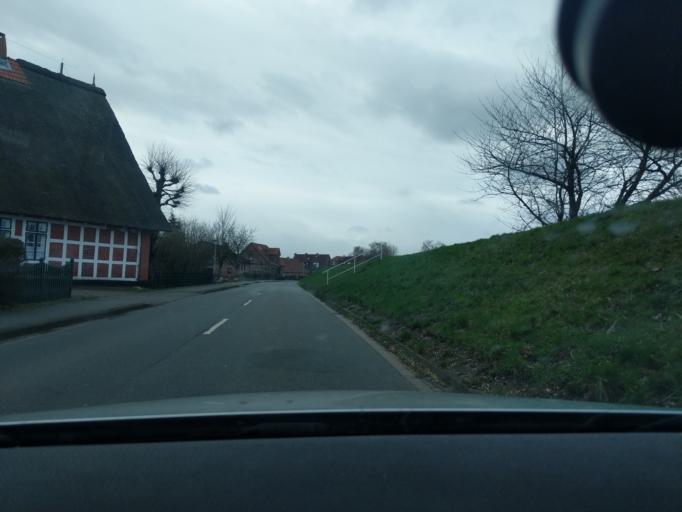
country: DE
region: Lower Saxony
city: Mittelnkirchen
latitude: 53.5385
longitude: 9.6170
